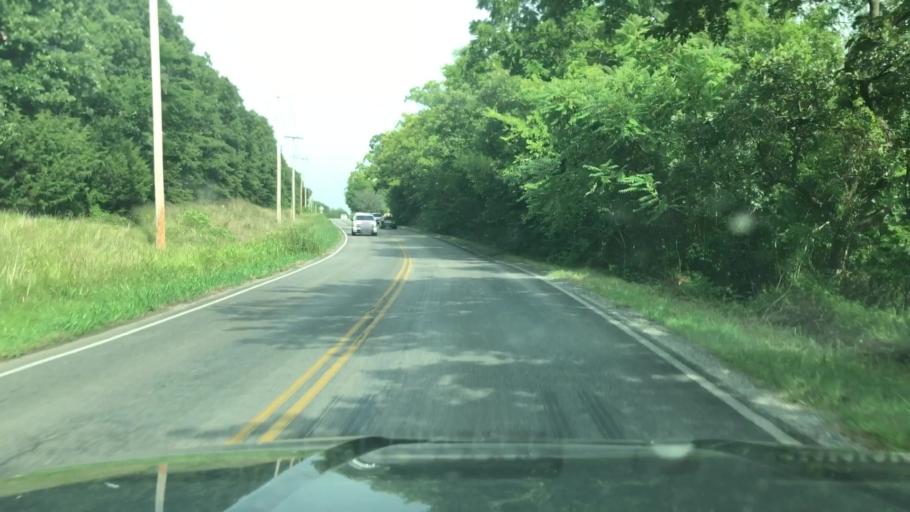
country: US
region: Oklahoma
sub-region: Tulsa County
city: Oakhurst
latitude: 36.0895
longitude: -96.0775
